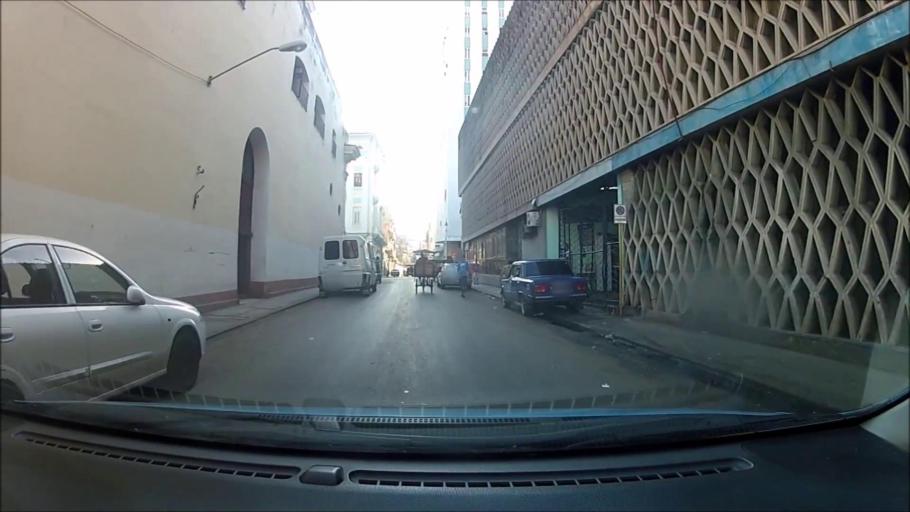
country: CU
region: La Habana
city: Centro Habana
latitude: 23.1385
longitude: -82.3642
